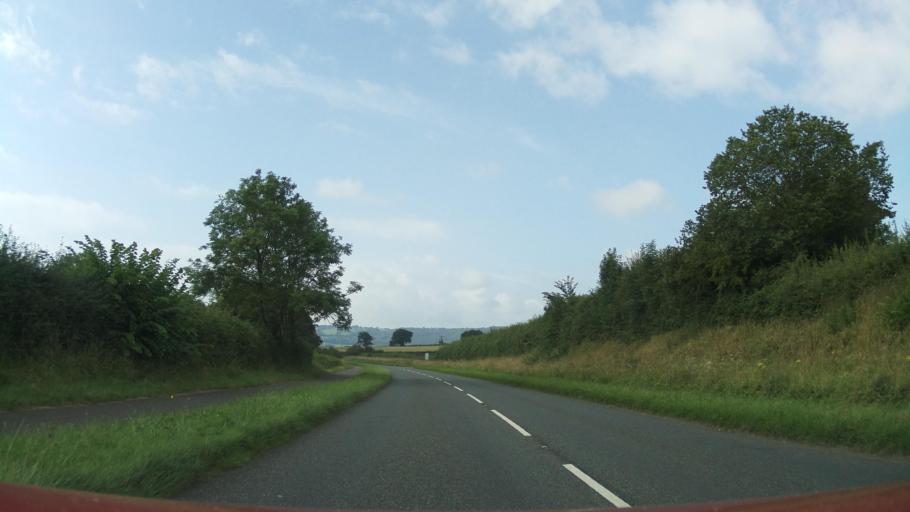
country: GB
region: England
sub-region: Bath and North East Somerset
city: Compton Martin
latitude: 51.3404
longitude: -2.6384
